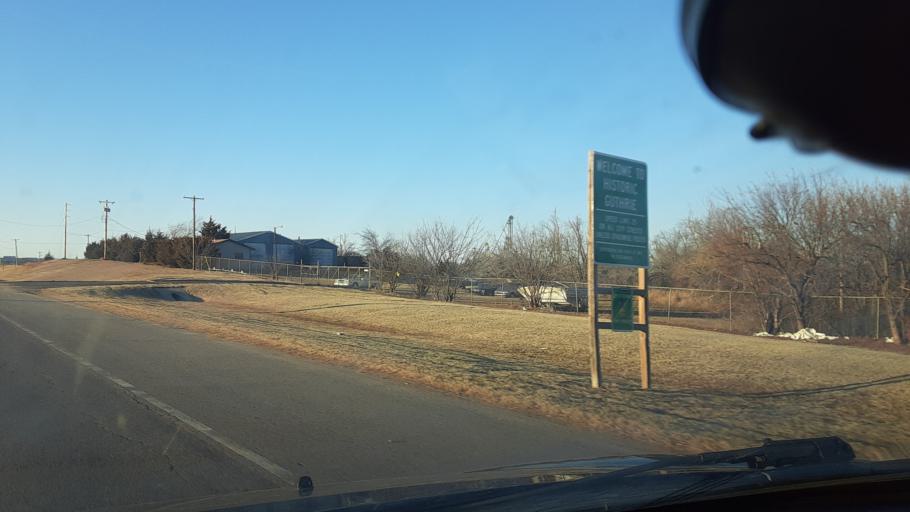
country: US
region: Oklahoma
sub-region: Logan County
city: Guthrie
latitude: 35.8251
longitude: -97.4210
